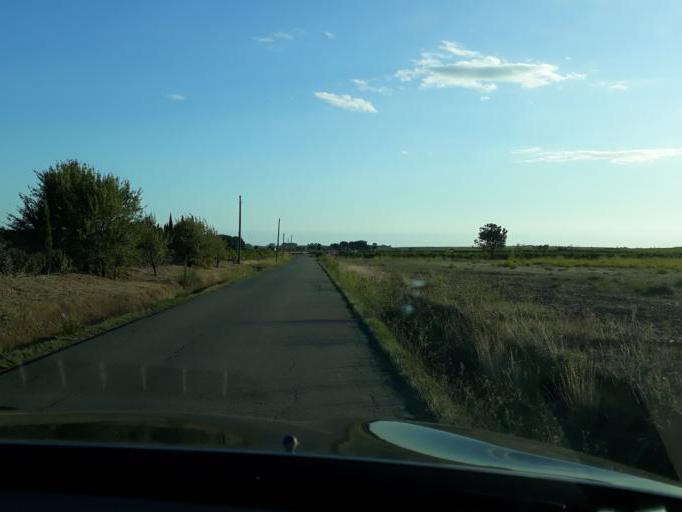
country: FR
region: Languedoc-Roussillon
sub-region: Departement de l'Herault
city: Pomerols
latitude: 43.3734
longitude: 3.4980
